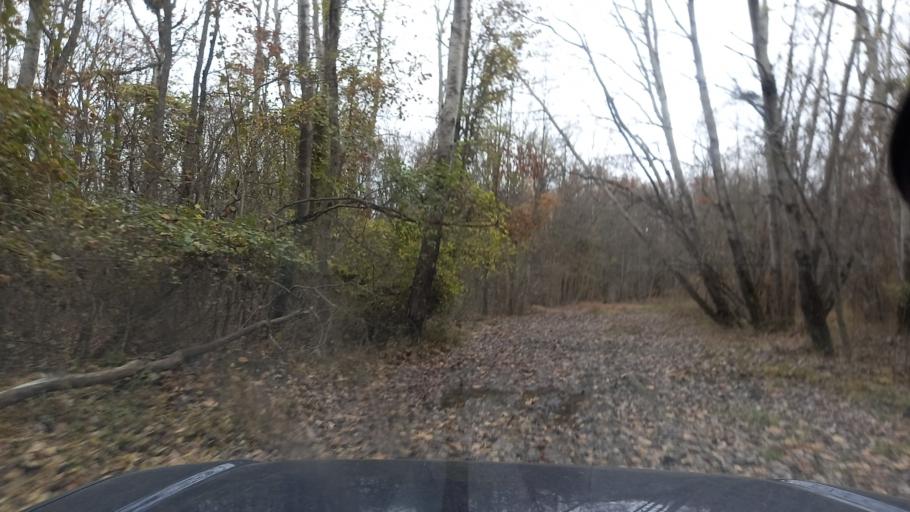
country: RU
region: Krasnodarskiy
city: Goryachiy Klyuch
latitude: 44.5068
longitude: 39.2902
